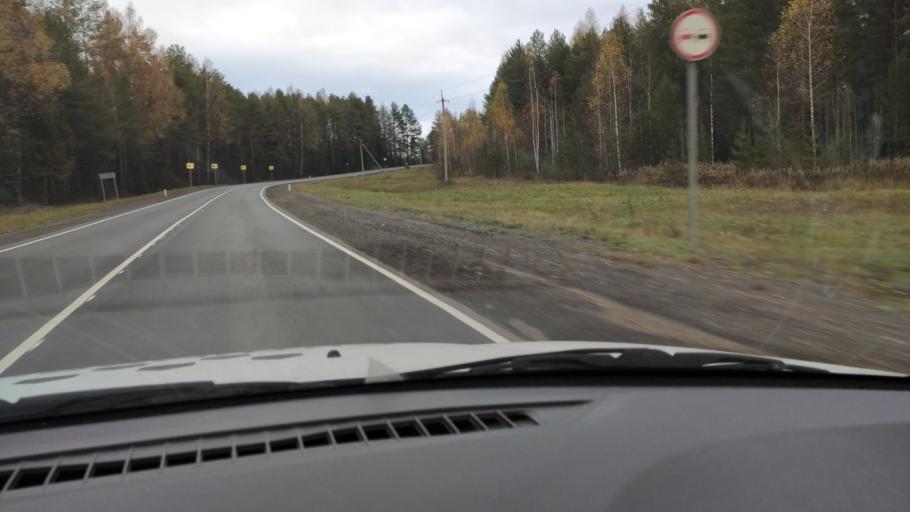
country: RU
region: Kirov
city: Belaya Kholunitsa
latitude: 58.8397
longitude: 50.6876
